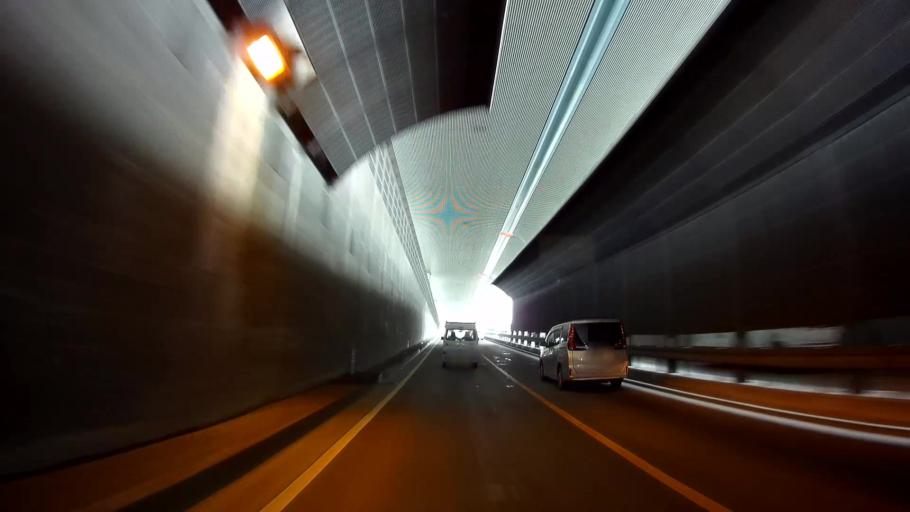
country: JP
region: Saitama
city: Yono
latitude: 35.8695
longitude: 139.6202
